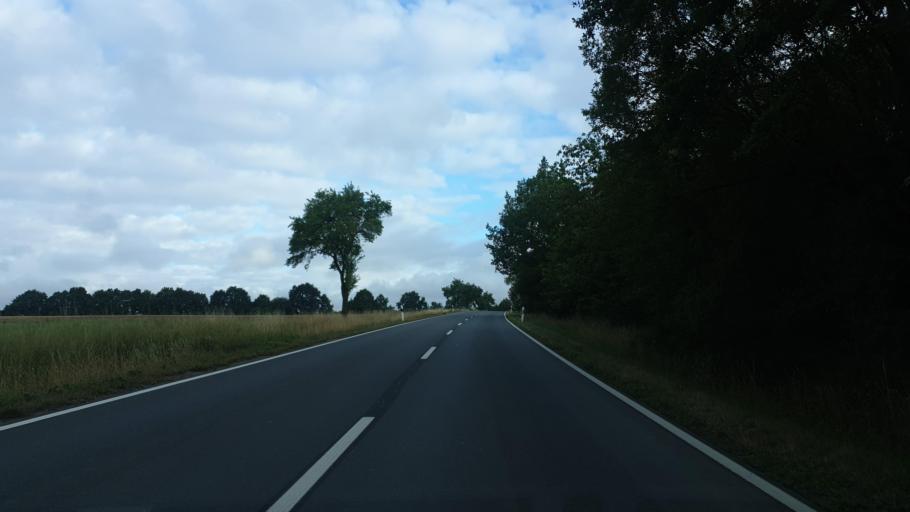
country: DE
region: Saxony
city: Limbach
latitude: 50.5793
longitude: 12.2300
